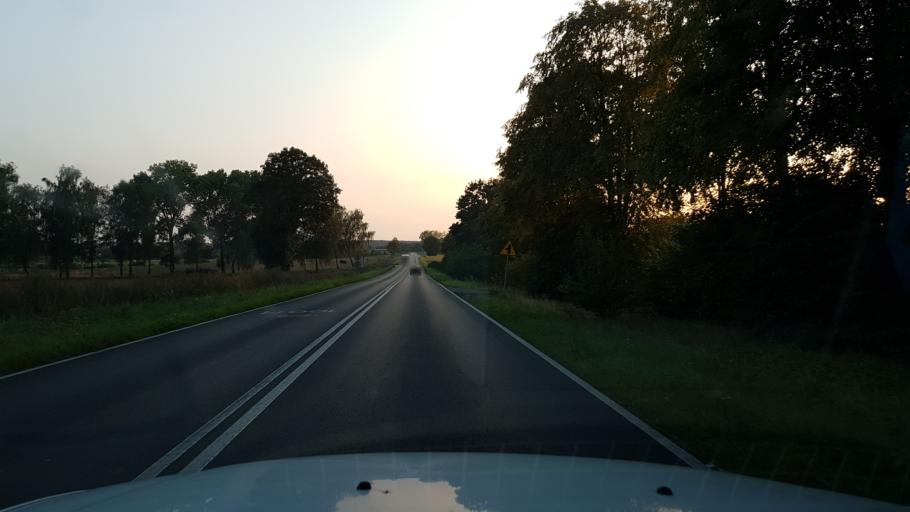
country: PL
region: West Pomeranian Voivodeship
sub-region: Powiat goleniowski
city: Nowogard
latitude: 53.6868
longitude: 15.1348
